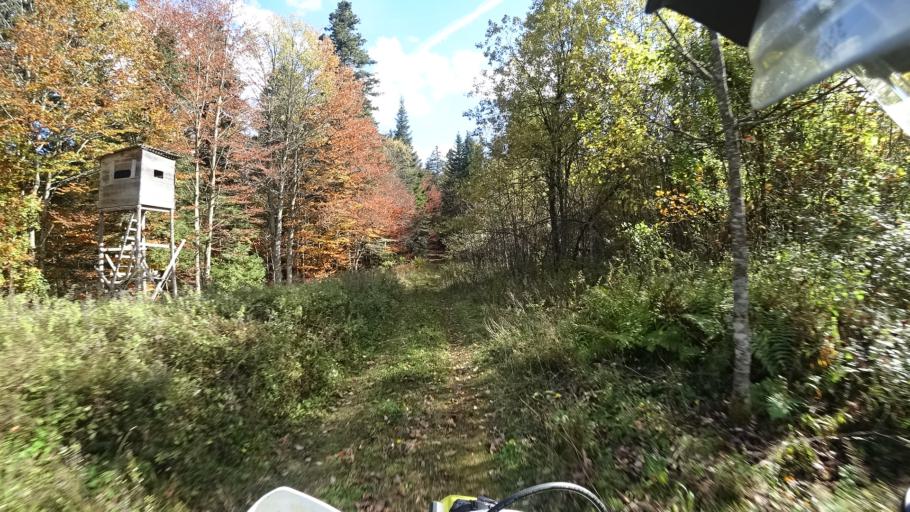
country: HR
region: Karlovacka
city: Plaski
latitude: 45.0682
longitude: 15.3130
